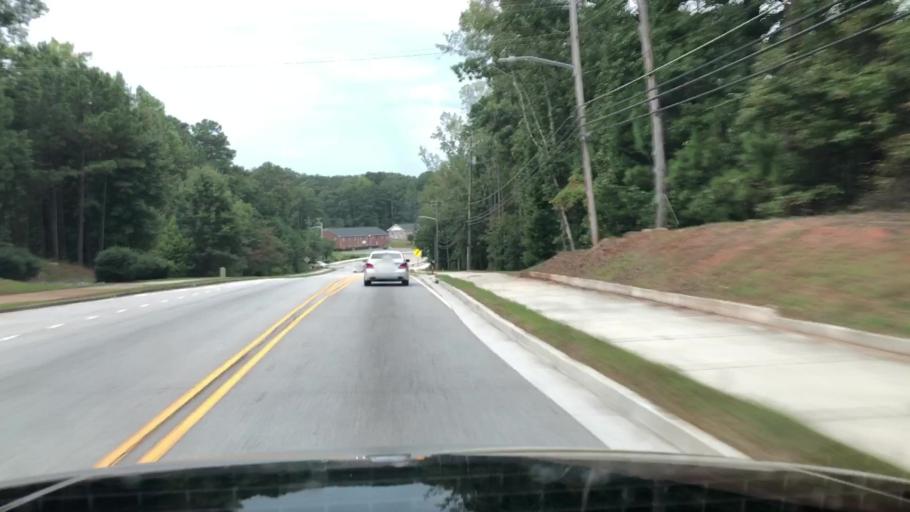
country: US
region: Georgia
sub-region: Cobb County
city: Mableton
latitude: 33.7040
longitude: -84.5633
